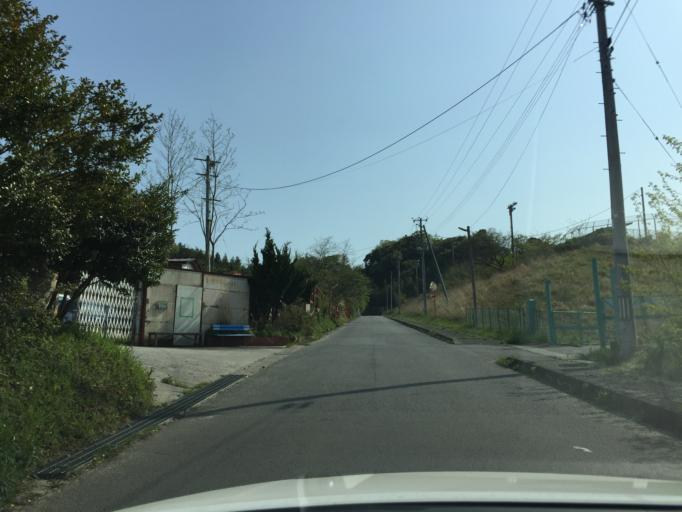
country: JP
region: Fukushima
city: Iwaki
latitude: 37.1383
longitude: 140.8738
